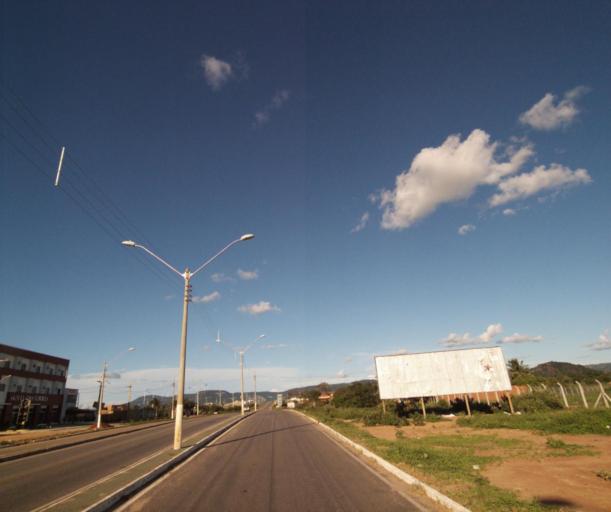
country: BR
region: Bahia
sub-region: Guanambi
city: Guanambi
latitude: -14.2026
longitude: -42.7573
